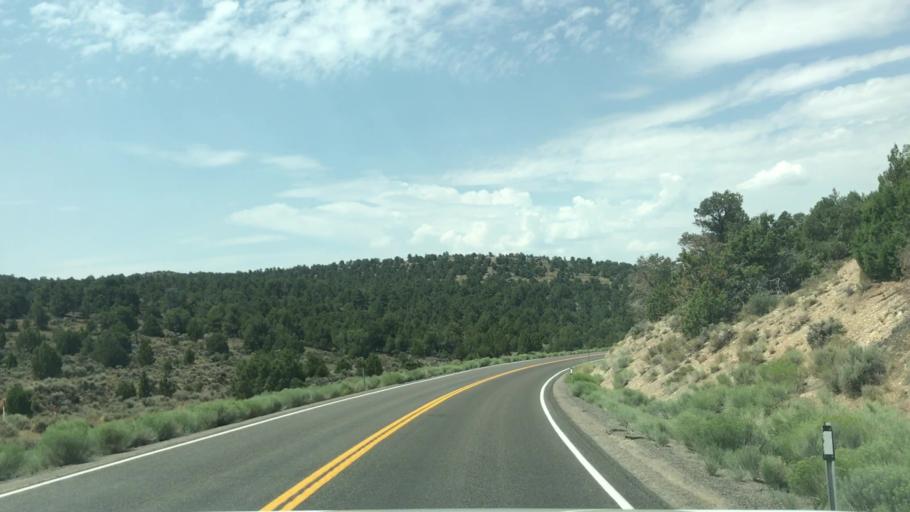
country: US
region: Nevada
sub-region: Eureka County
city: Eureka
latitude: 39.3960
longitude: -115.4771
